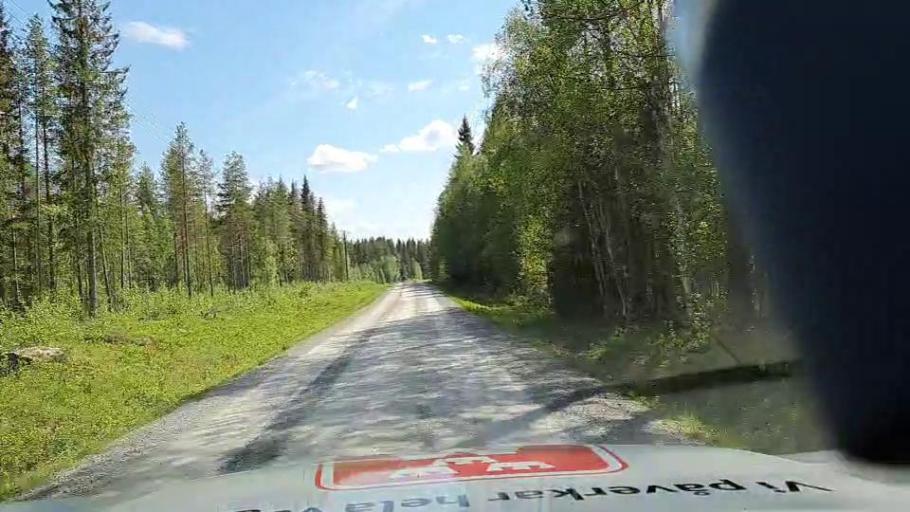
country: SE
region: Jaemtland
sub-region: Stroemsunds Kommun
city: Stroemsund
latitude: 64.4691
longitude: 15.5944
